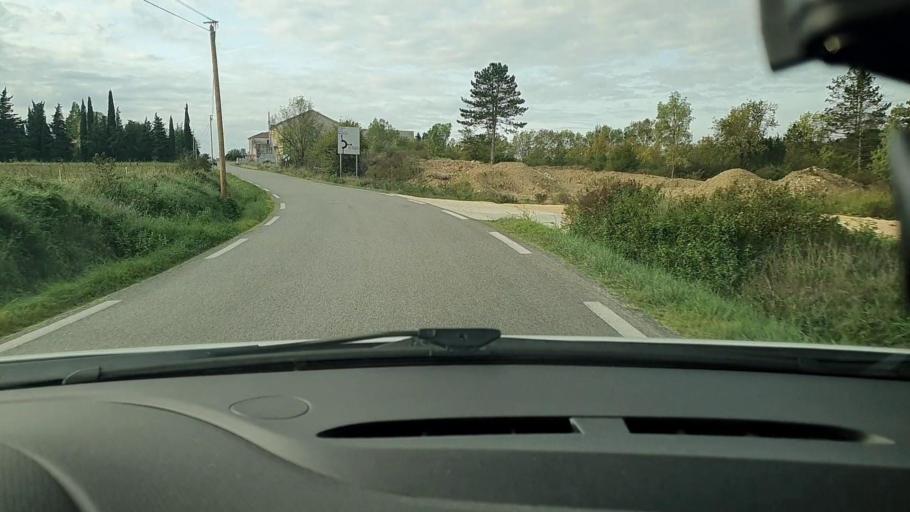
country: FR
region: Languedoc-Roussillon
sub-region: Departement du Gard
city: Salindres
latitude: 44.1865
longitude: 4.2349
